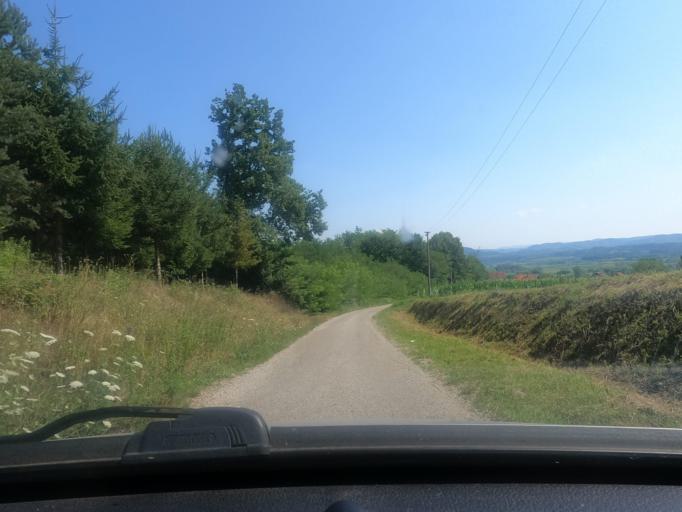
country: RS
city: Jarebice
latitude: 44.5407
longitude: 19.3767
